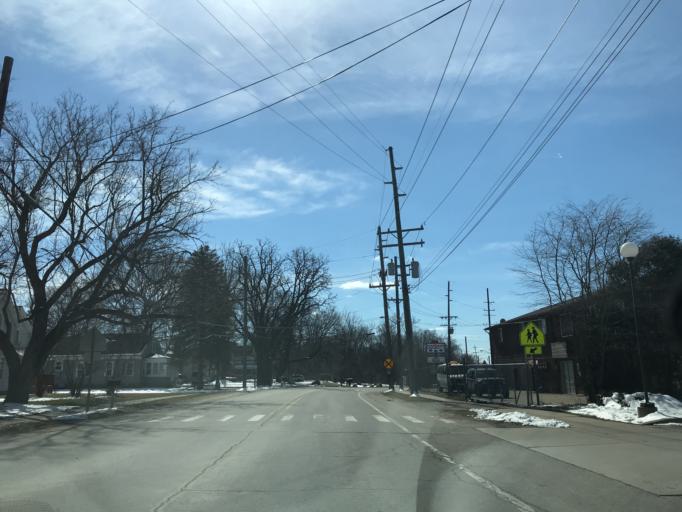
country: US
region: Michigan
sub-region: Livingston County
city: Whitmore Lake
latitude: 42.4171
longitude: -83.7605
